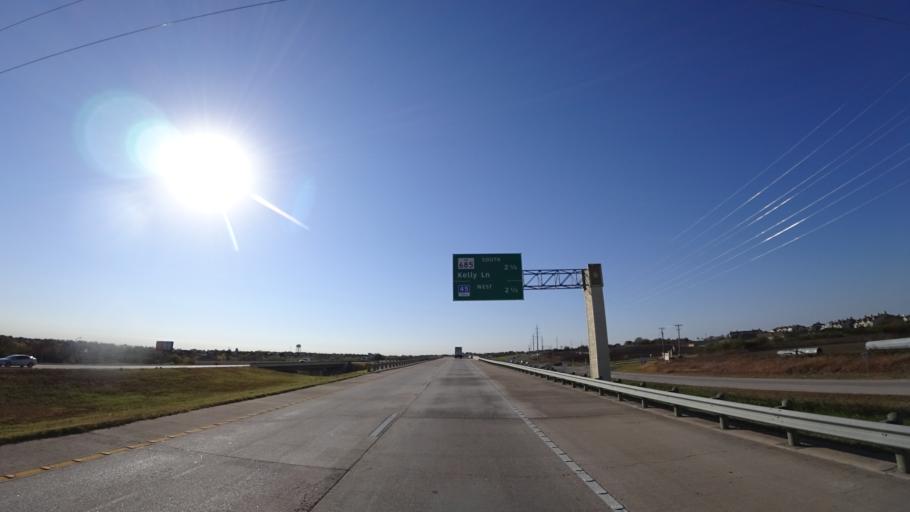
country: US
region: Texas
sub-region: Williamson County
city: Hutto
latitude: 30.5149
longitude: -97.5758
